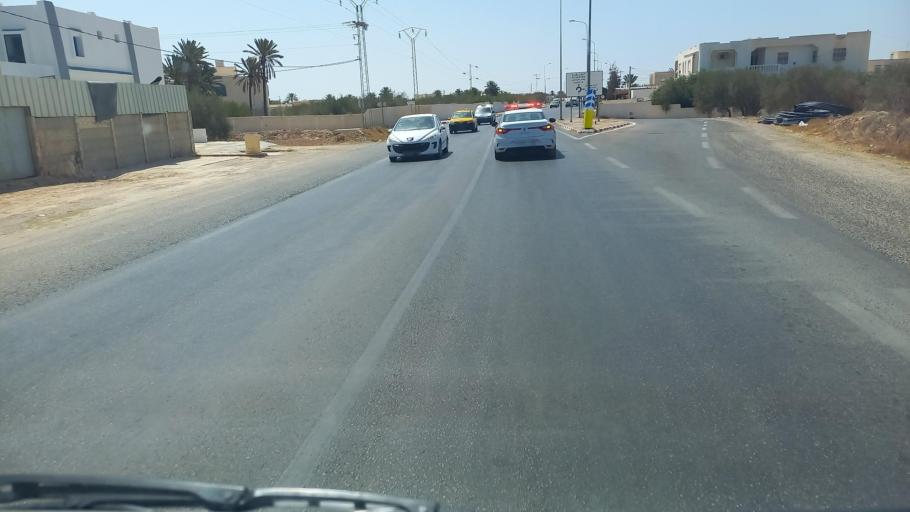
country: TN
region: Madanin
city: Houmt Souk
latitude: 33.8252
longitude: 10.8705
